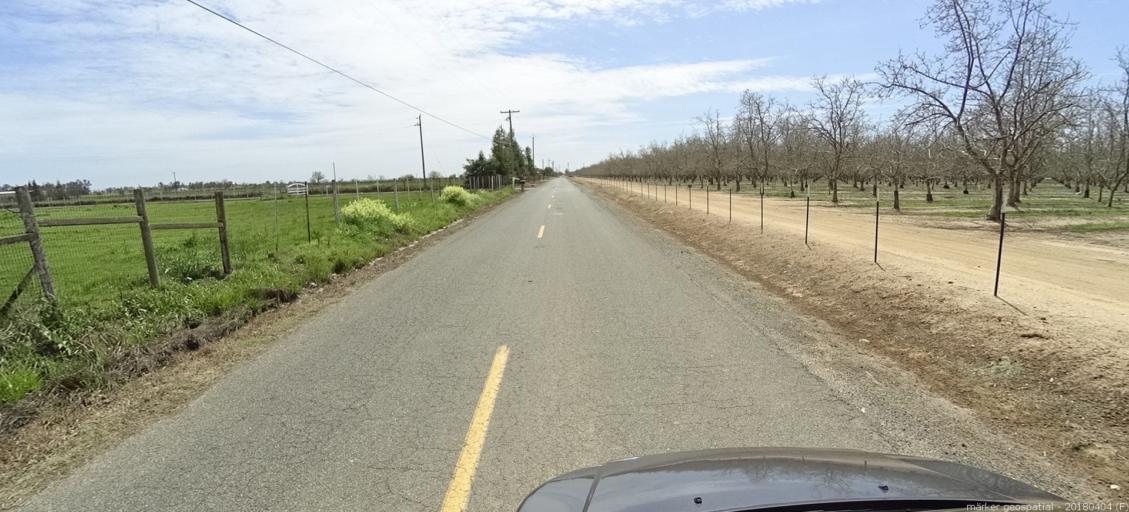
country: US
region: California
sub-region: Sacramento County
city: Herald
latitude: 38.3002
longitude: -121.2080
